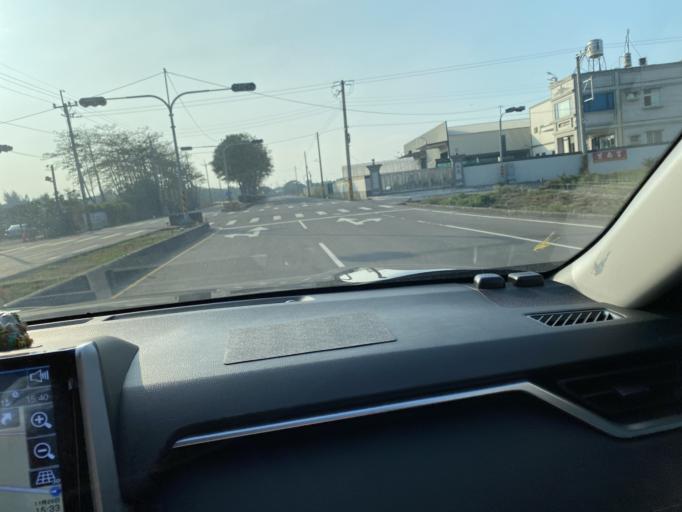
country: TW
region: Taiwan
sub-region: Changhua
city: Chang-hua
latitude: 23.9612
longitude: 120.3879
